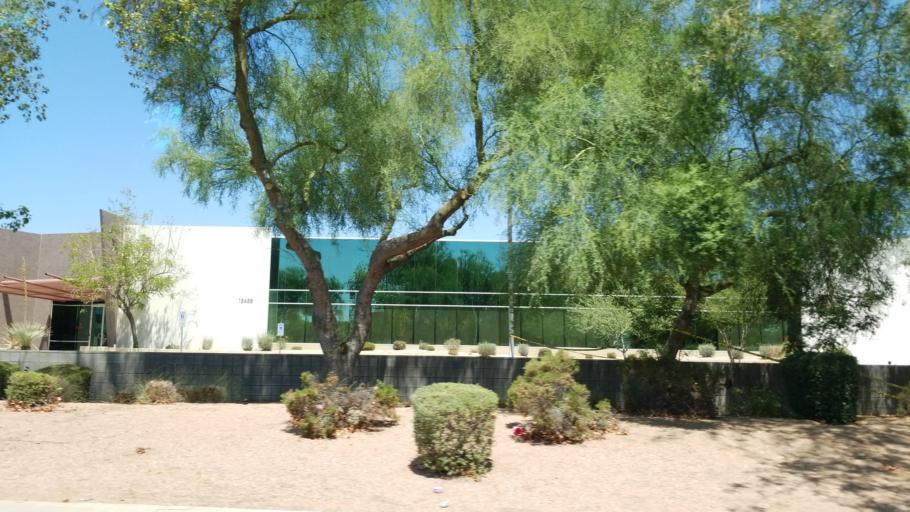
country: US
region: Arizona
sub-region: Maricopa County
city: Glendale
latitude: 33.6268
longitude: -112.1189
